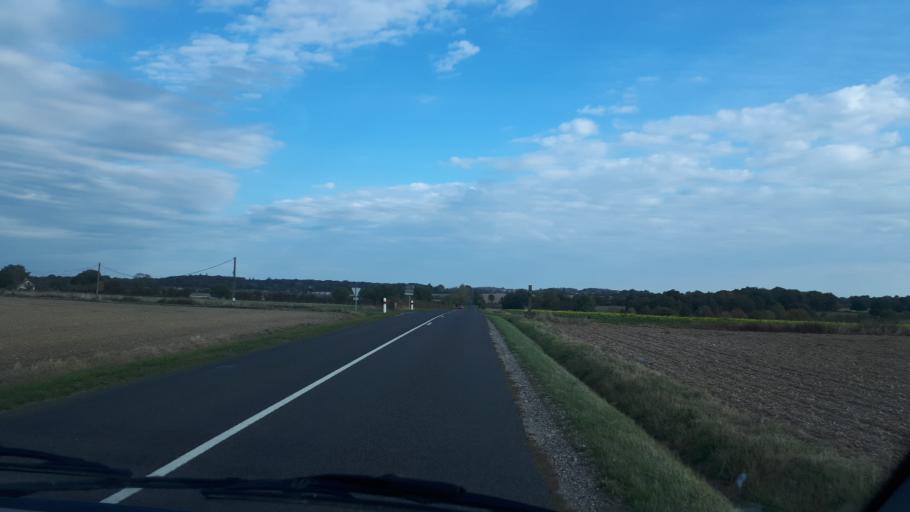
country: FR
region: Centre
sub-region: Departement du Loir-et-Cher
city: Mondoubleau
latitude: 47.9140
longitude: 0.9313
